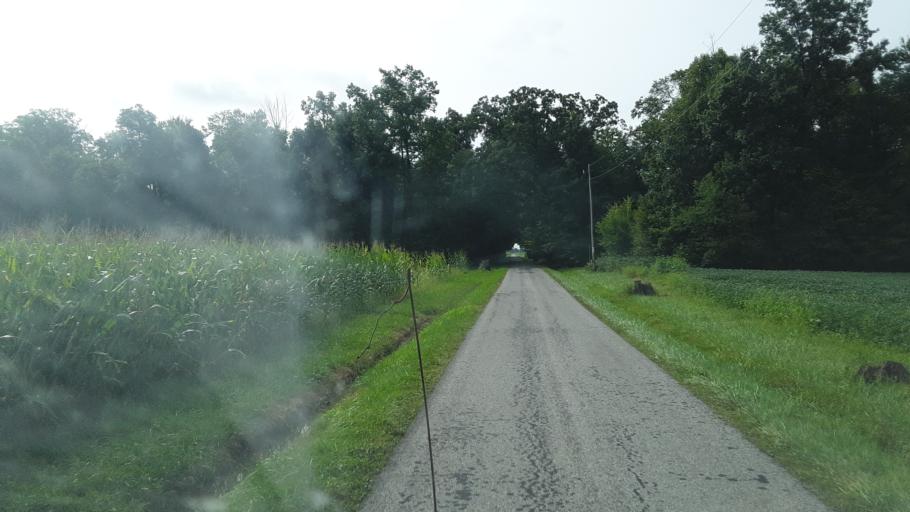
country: US
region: Ohio
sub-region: Morrow County
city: Cardington
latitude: 40.5224
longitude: -82.9770
